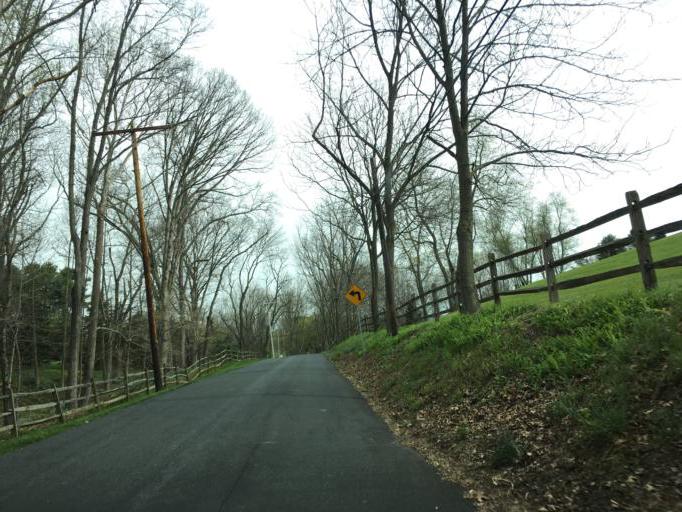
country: US
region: Maryland
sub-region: Baltimore County
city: Hunt Valley
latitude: 39.5585
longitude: -76.6042
